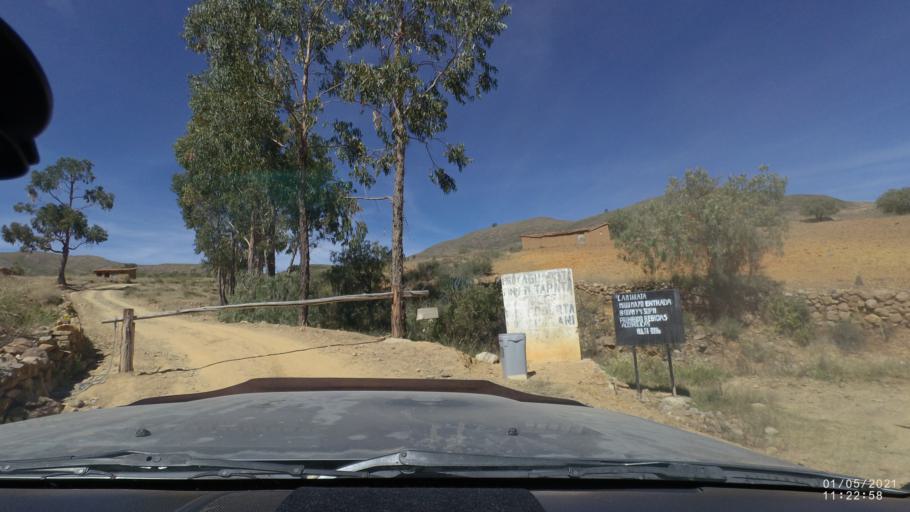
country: BO
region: Cochabamba
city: Tarata
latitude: -17.6507
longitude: -66.1322
